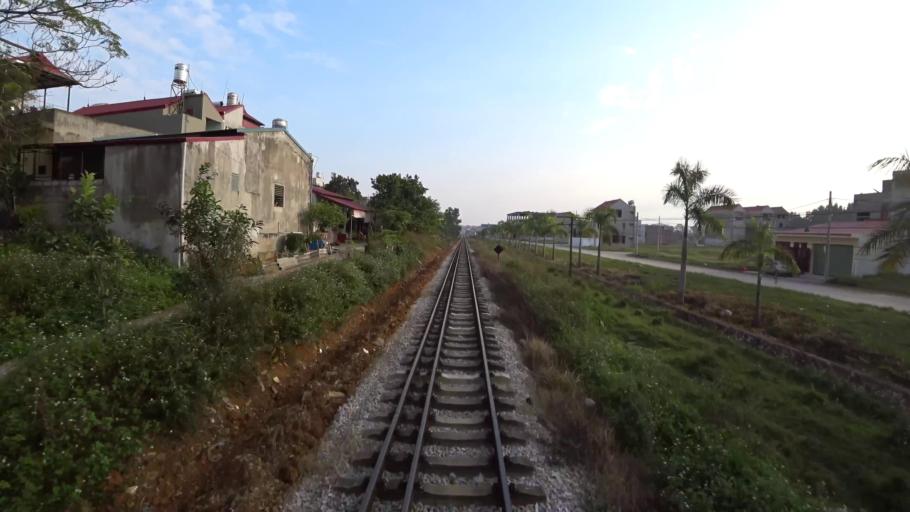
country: VN
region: Lang Son
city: Thi Tran Cao Loc
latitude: 21.8829
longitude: 106.7485
